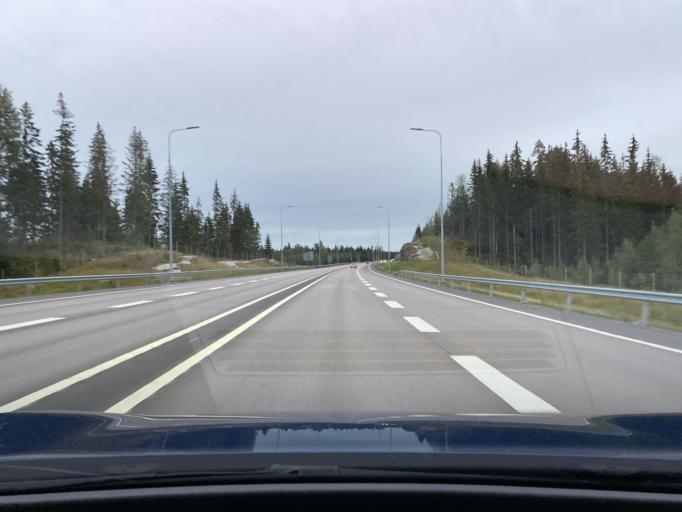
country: FI
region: Paijanne Tavastia
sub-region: Lahti
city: Hollola
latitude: 60.9783
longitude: 25.4944
